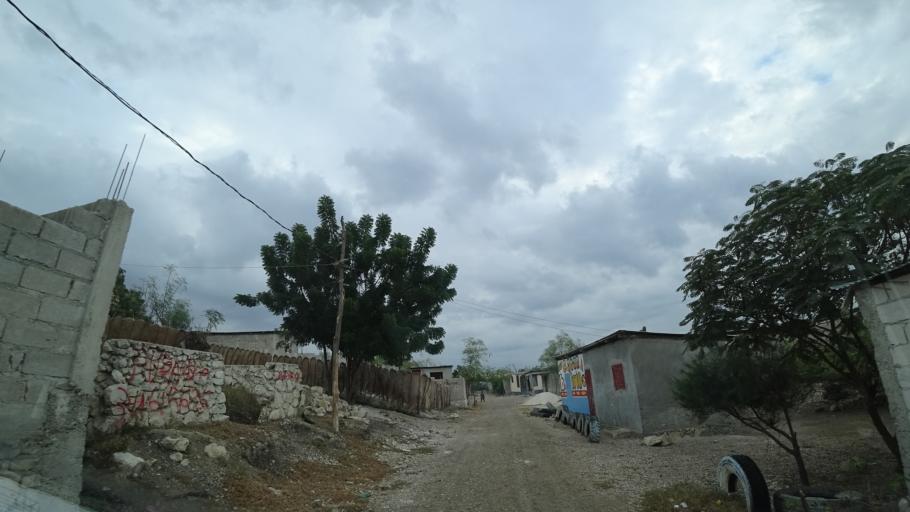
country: HT
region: Ouest
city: Croix des Bouquets
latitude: 18.6496
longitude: -72.2793
